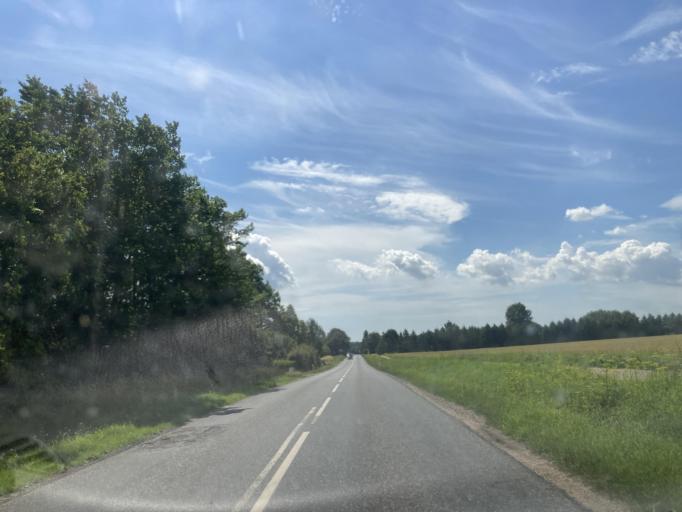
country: DK
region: Zealand
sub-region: Faxe Kommune
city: Haslev
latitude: 55.3731
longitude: 11.9636
